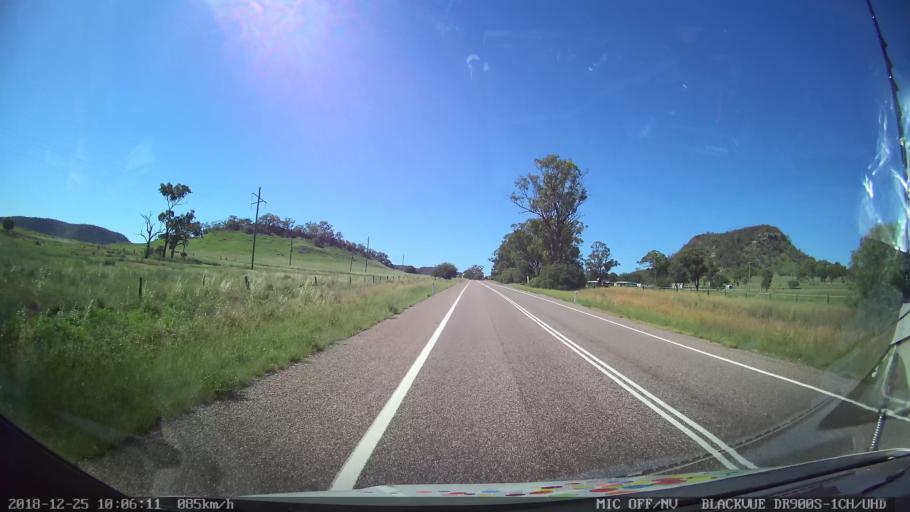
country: AU
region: New South Wales
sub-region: Upper Hunter Shire
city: Merriwa
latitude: -32.2569
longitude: 150.4890
